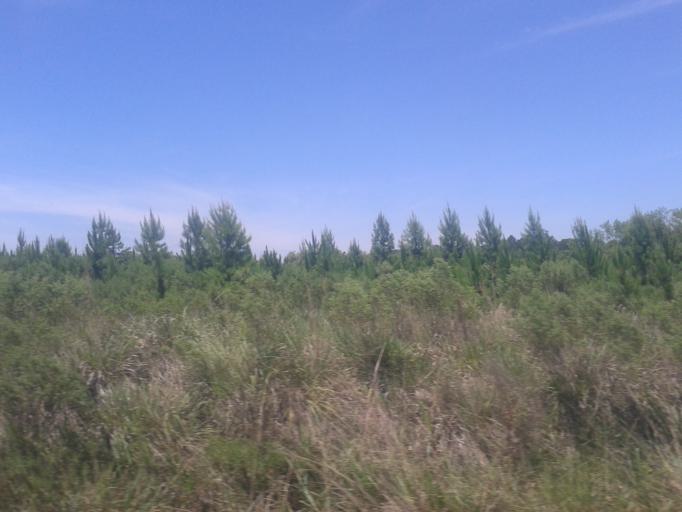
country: AR
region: Misiones
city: Bonpland
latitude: -27.4226
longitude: -55.5172
